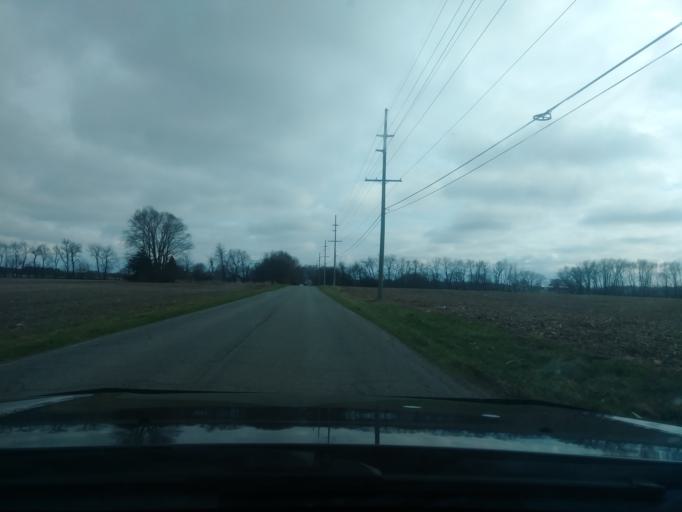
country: US
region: Indiana
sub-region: LaPorte County
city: LaPorte
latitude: 41.6206
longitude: -86.7964
